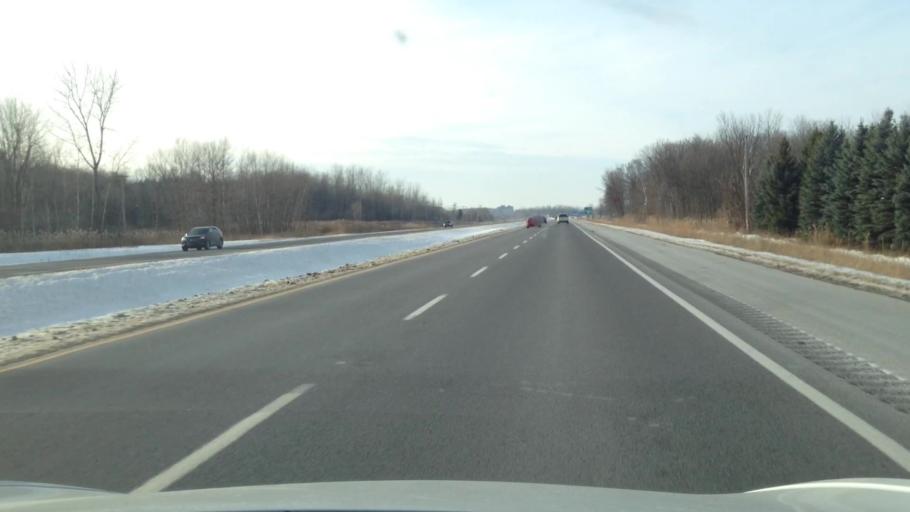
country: CA
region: Quebec
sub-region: Monteregie
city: Rigaud
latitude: 45.4707
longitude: -74.2567
